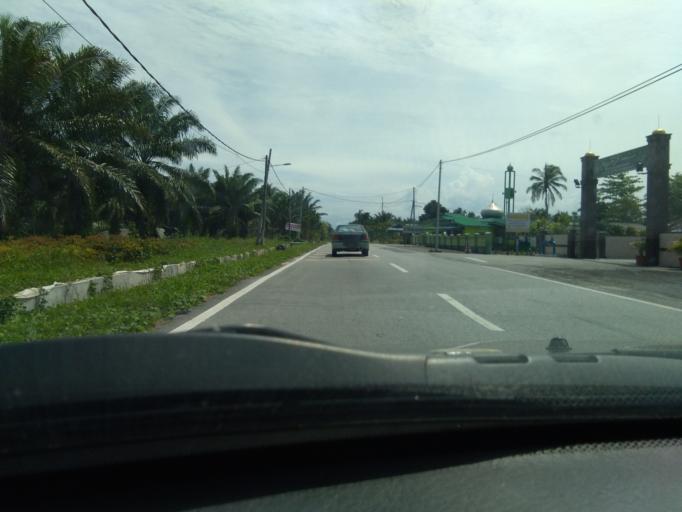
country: MY
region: Perak
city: Bagan Serai
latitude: 5.0231
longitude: 100.5506
